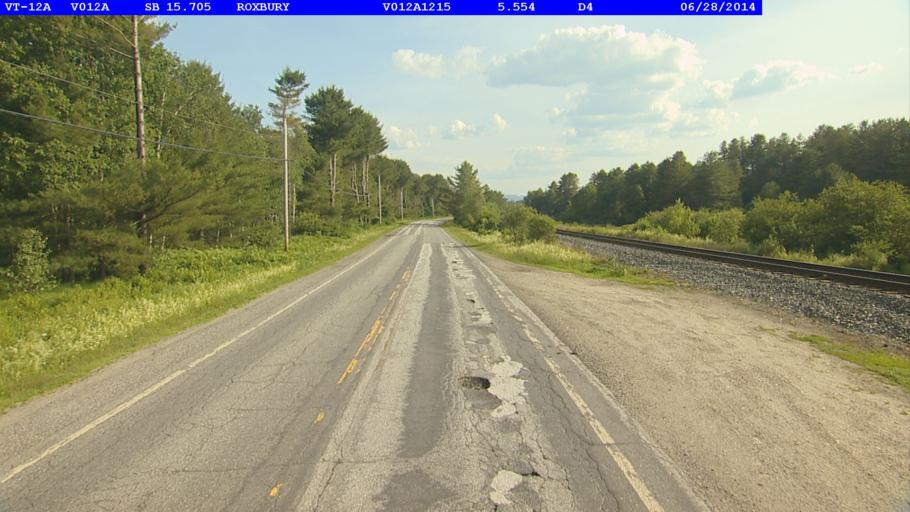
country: US
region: Vermont
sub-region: Washington County
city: Northfield
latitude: 44.1051
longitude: -72.7293
